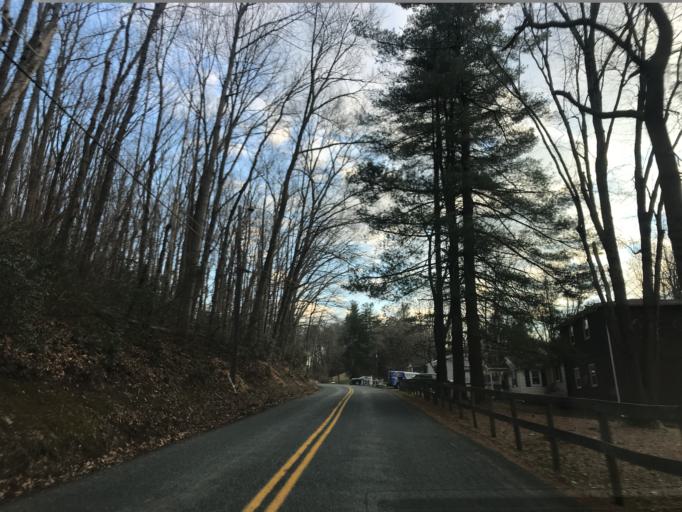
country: US
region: Maryland
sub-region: Harford County
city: Jarrettsville
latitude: 39.6265
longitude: -76.4200
